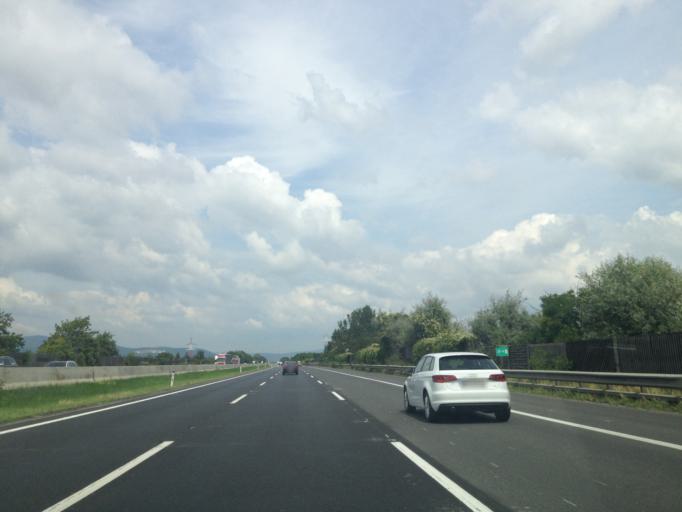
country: AT
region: Lower Austria
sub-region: Politischer Bezirk Wiener Neustadt
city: Felixdorf
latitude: 47.8908
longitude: 16.2070
